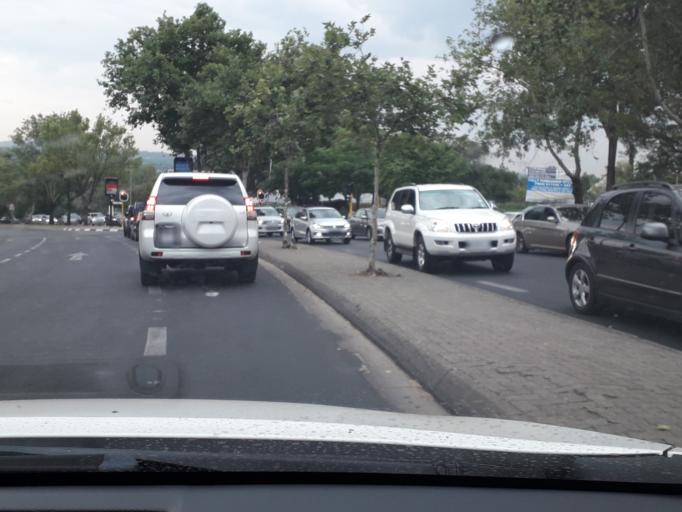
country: ZA
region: Gauteng
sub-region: City of Johannesburg Metropolitan Municipality
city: Johannesburg
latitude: -26.1011
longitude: 28.0496
